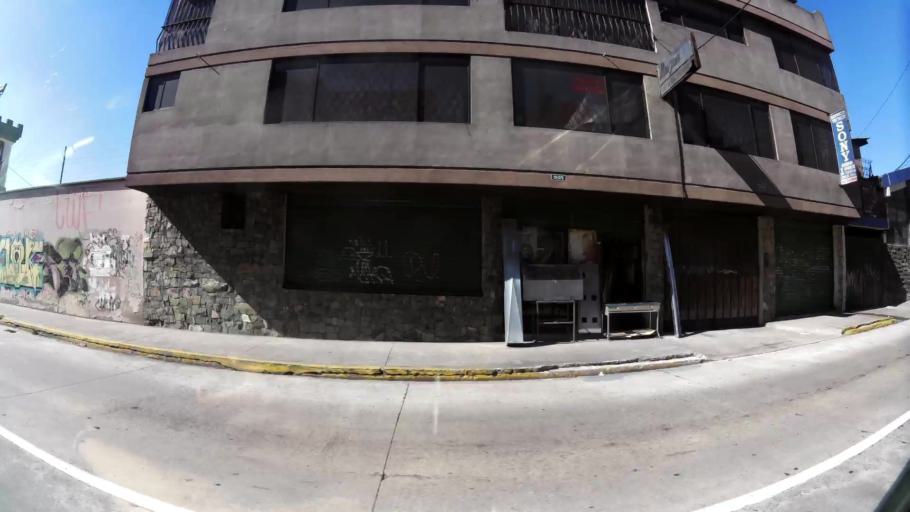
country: EC
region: Pichincha
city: Quito
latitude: -0.2359
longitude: -78.5256
